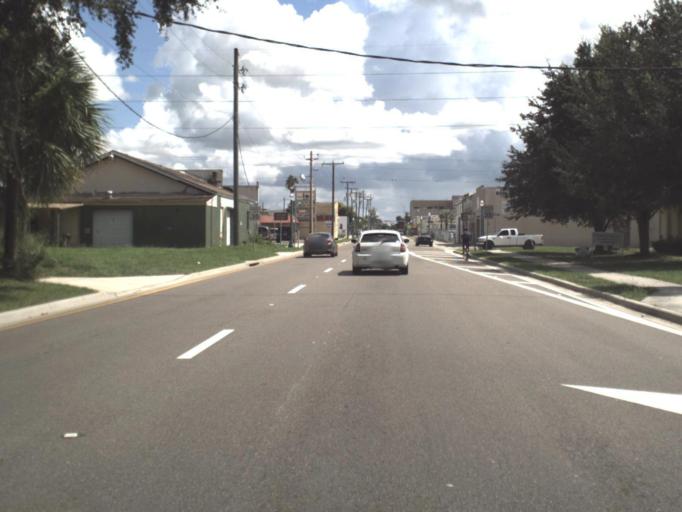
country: US
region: Florida
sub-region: DeSoto County
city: Arcadia
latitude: 27.2158
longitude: -81.8649
